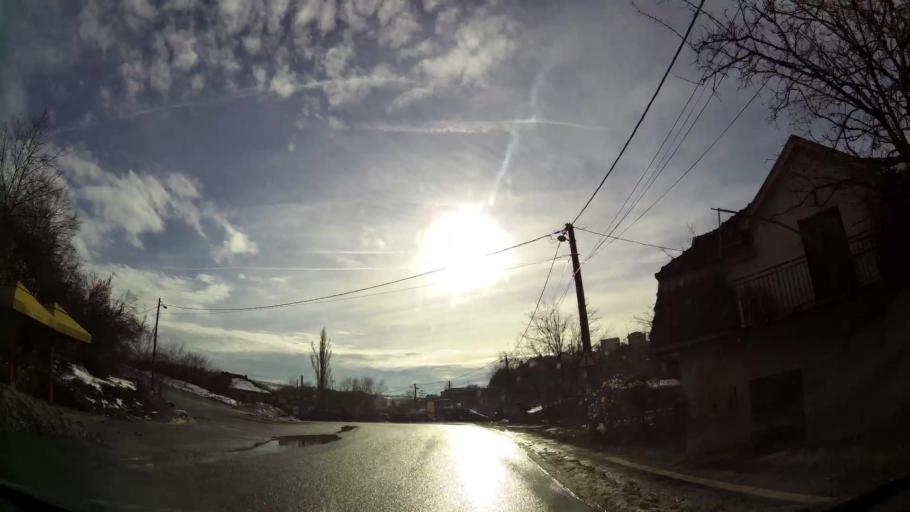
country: RS
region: Central Serbia
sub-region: Belgrade
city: Rakovica
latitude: 44.7255
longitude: 20.4384
